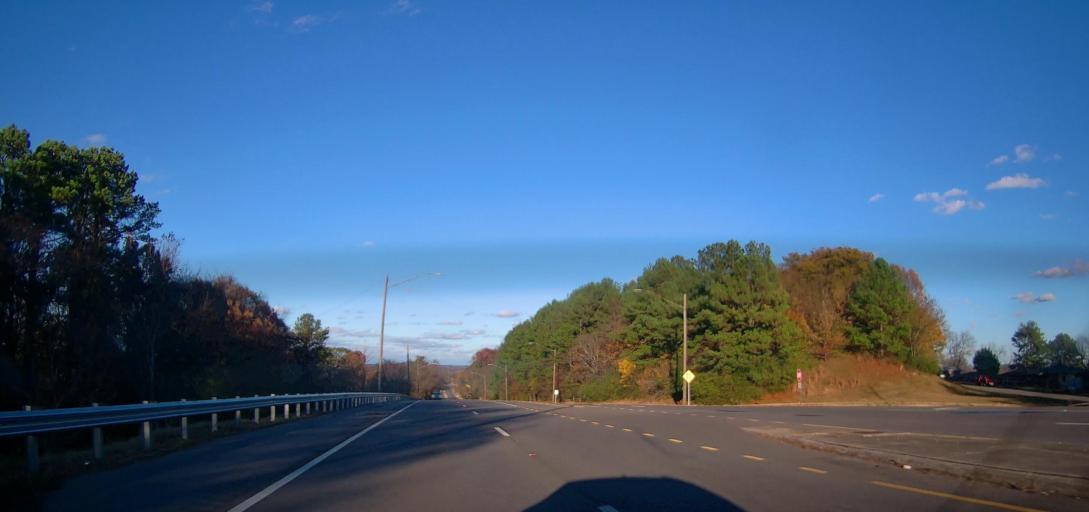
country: US
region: Alabama
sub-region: Jefferson County
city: Fultondale
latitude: 33.5656
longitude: -86.8164
